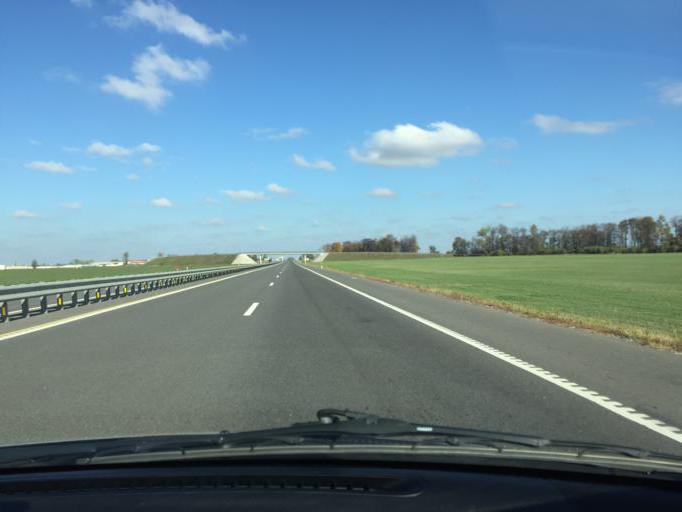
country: BY
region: Minsk
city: Slutsk
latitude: 53.0634
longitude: 27.5485
